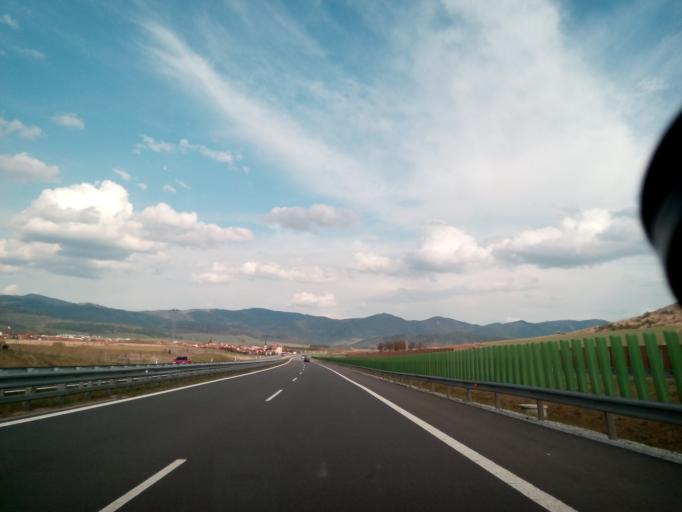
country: SK
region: Presovsky
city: Spisske Podhradie
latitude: 49.0078
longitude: 20.7519
